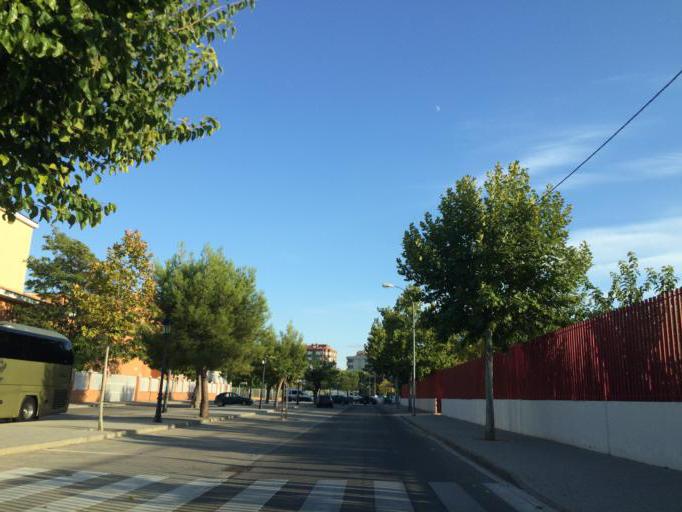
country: ES
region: Castille-La Mancha
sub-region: Provincia de Albacete
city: Albacete
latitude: 39.0066
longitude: -1.8639
